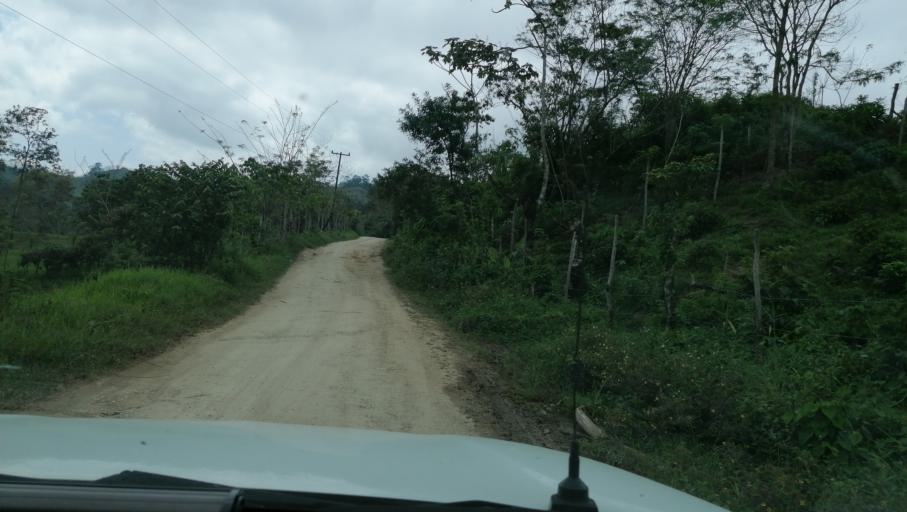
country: MX
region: Chiapas
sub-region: Ocotepec
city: San Pablo Huacano
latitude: 17.2750
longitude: -93.2350
